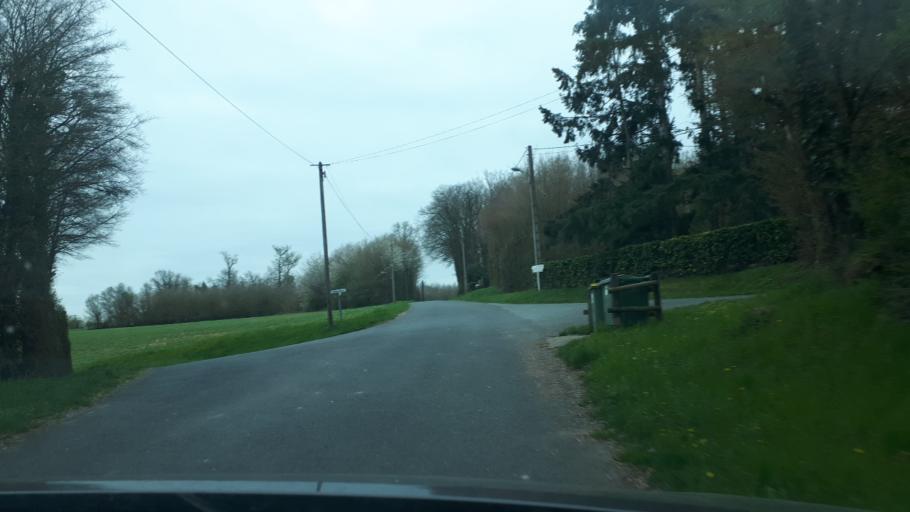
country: FR
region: Centre
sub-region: Departement du Loir-et-Cher
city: Lunay
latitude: 47.7489
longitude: 0.9472
